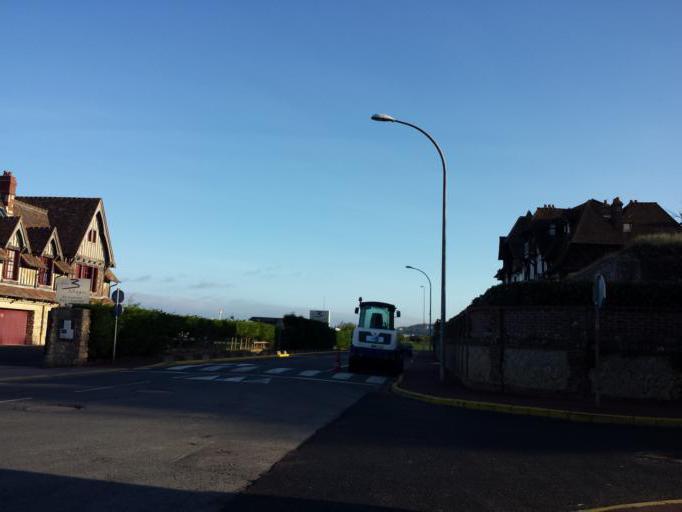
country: FR
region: Lower Normandy
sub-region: Departement du Calvados
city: Deauville
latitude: 49.3541
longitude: 0.0572
